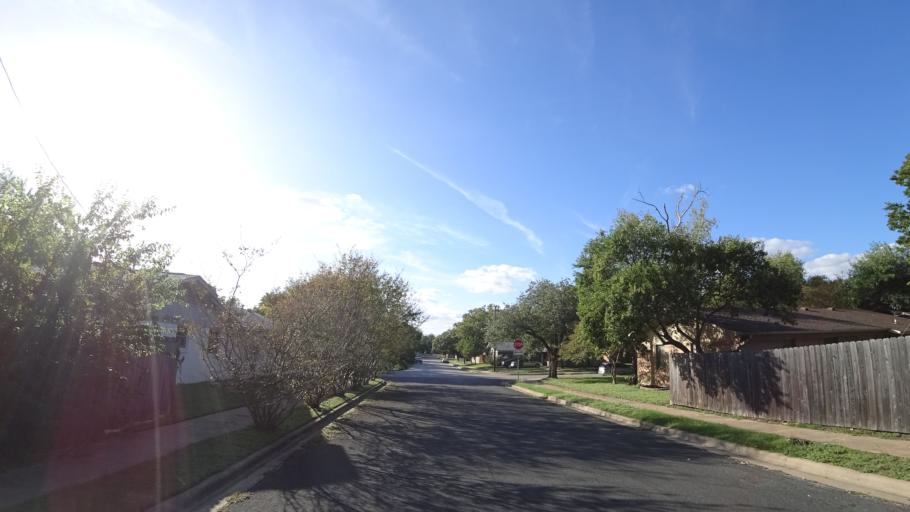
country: US
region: Texas
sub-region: Williamson County
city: Jollyville
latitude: 30.3663
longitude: -97.7316
